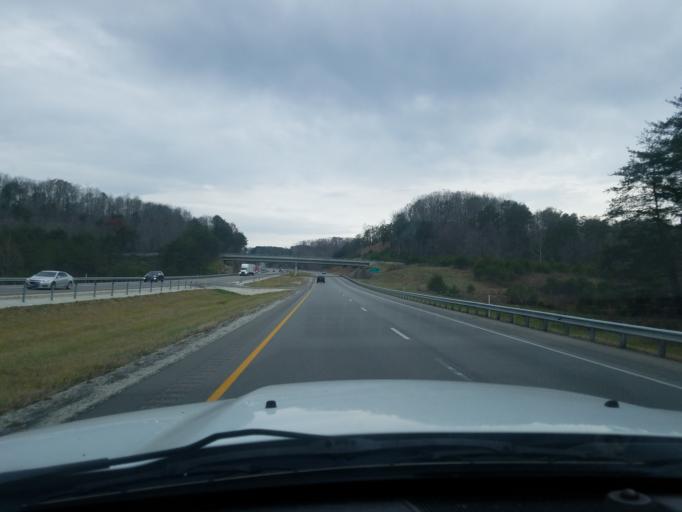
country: US
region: Kentucky
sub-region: Carter County
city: Grayson
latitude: 38.3705
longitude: -82.8374
